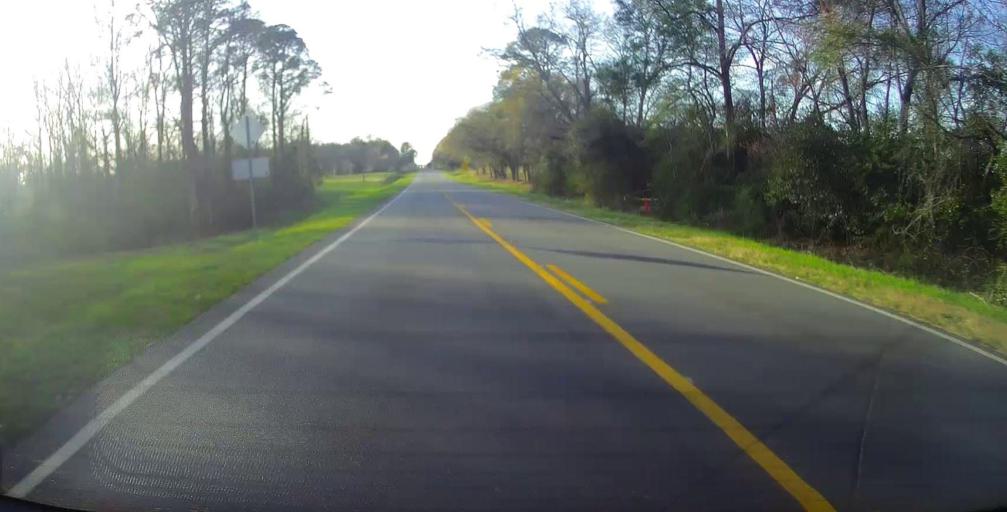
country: US
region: Georgia
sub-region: Evans County
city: Claxton
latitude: 32.1532
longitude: -81.8496
